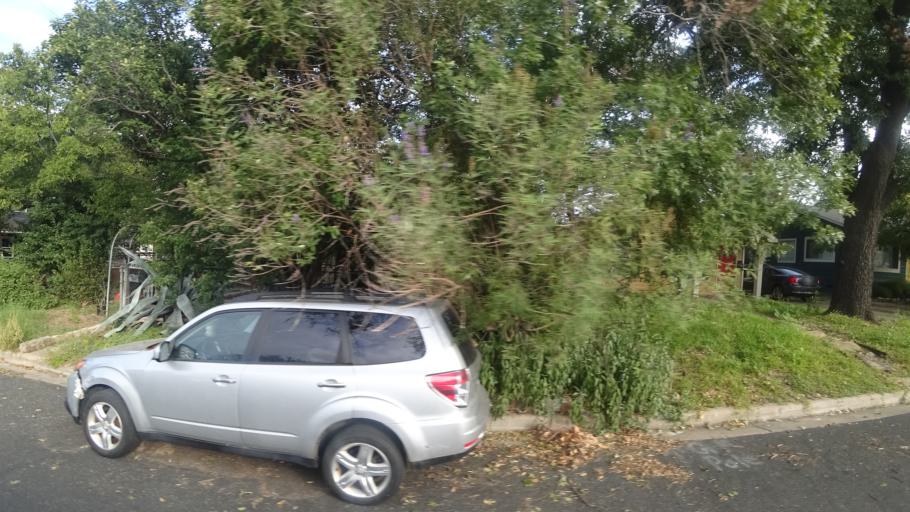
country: US
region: Texas
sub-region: Travis County
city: Austin
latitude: 30.2816
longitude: -97.7053
